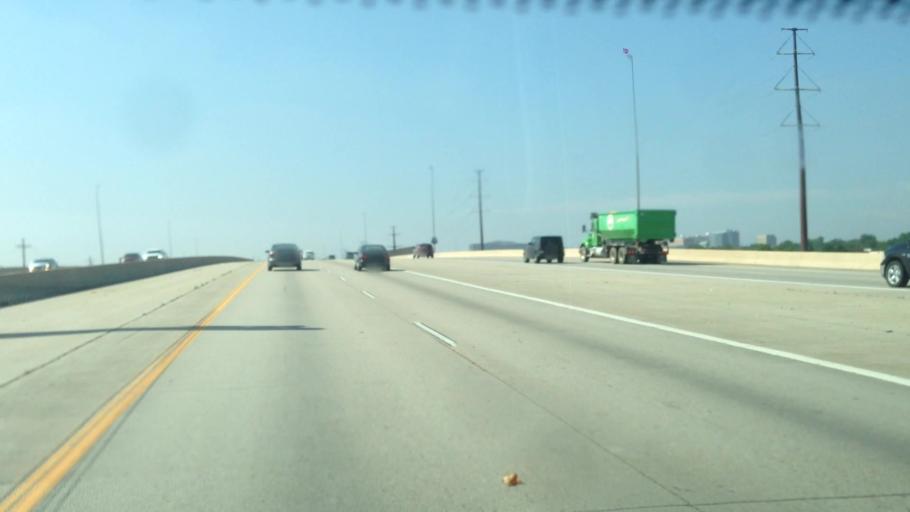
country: US
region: Colorado
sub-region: Adams County
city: Aurora
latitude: 39.7663
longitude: -104.8276
